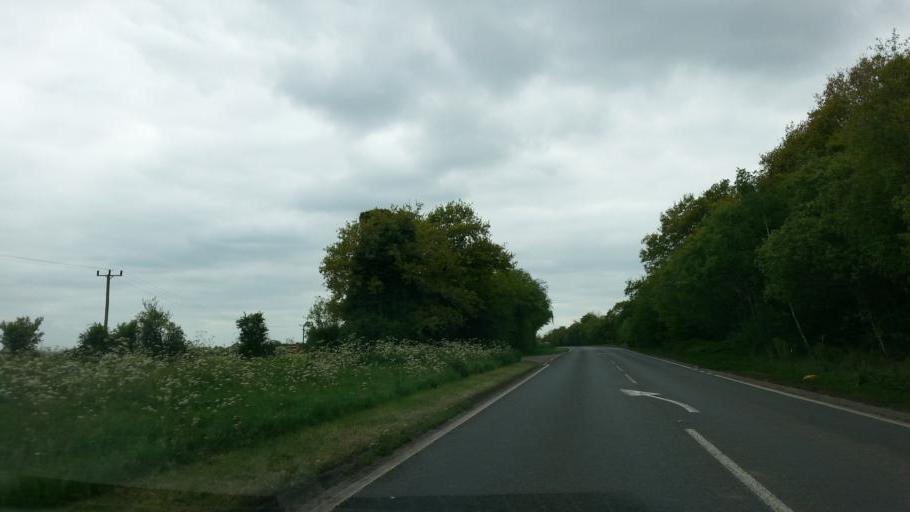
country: GB
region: England
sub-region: Suffolk
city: Hadleigh
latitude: 52.0534
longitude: 0.9971
